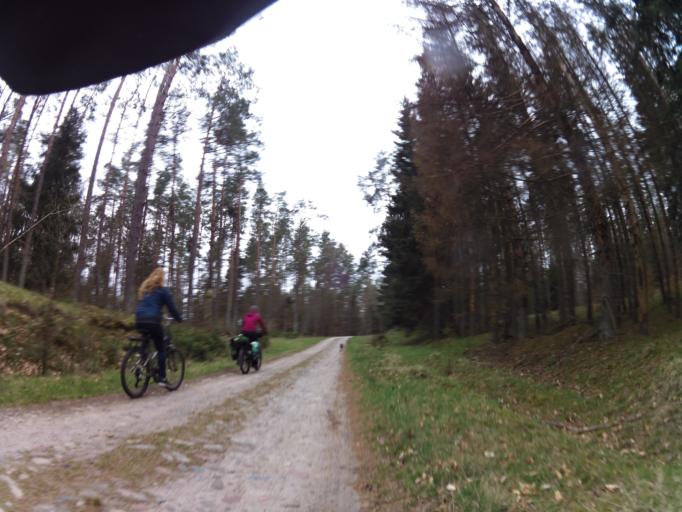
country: PL
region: West Pomeranian Voivodeship
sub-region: Powiat szczecinecki
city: Bialy Bor
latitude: 53.9395
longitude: 16.7233
